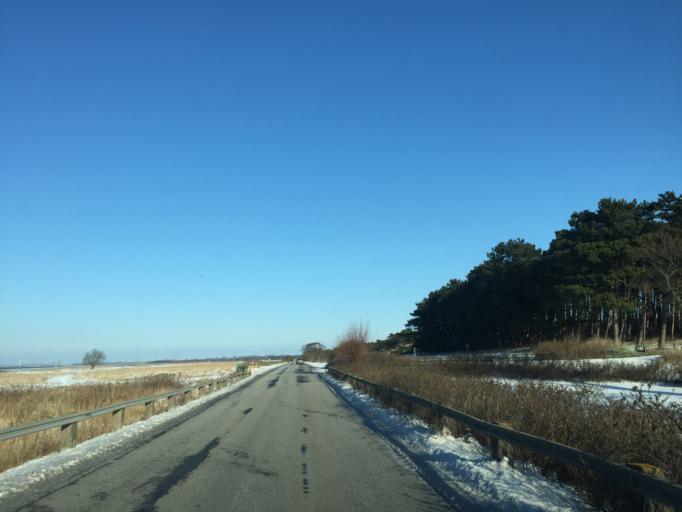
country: SE
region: Skane
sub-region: Kavlinge Kommun
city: Hofterup
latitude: 55.7899
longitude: 12.9383
